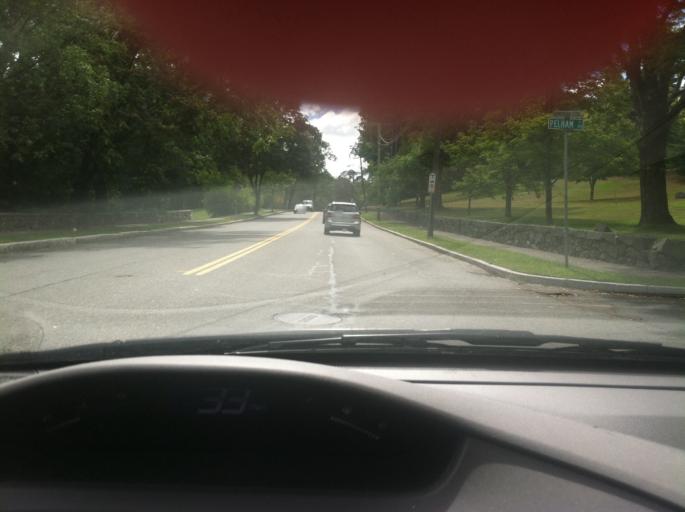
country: US
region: Massachusetts
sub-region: Middlesex County
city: Lexington
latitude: 42.4401
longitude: -71.2139
